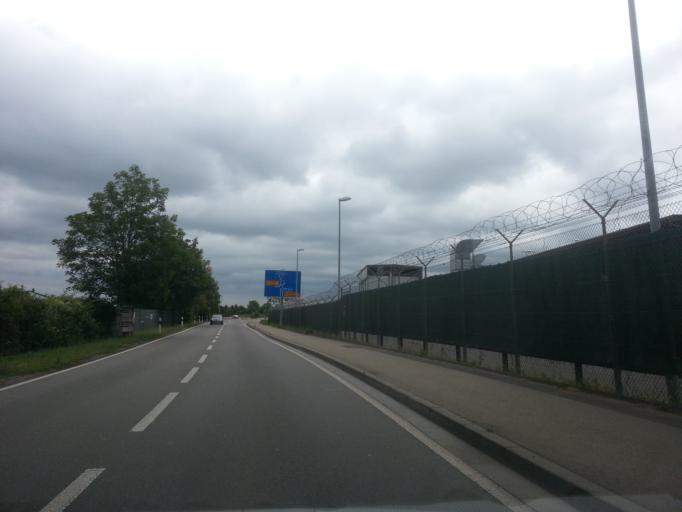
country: DE
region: Rheinland-Pfalz
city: Grunstadt
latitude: 49.5548
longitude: 8.1782
